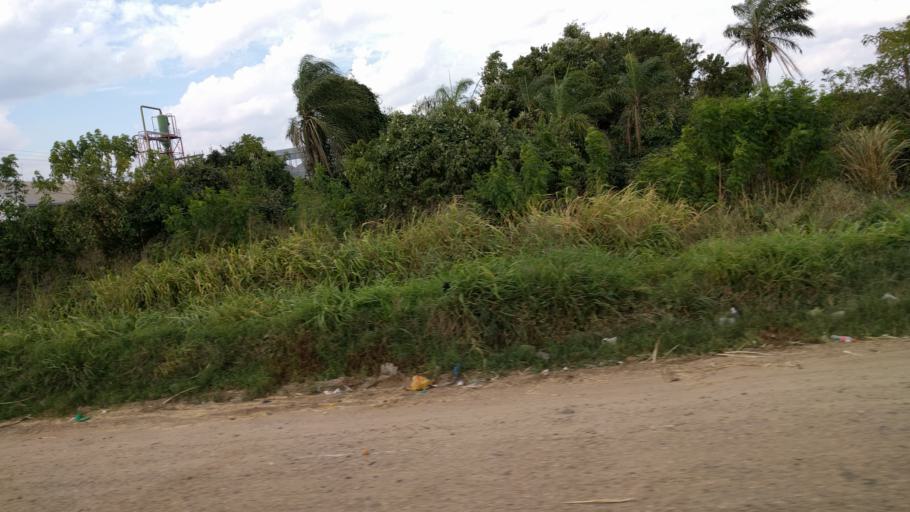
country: BO
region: Santa Cruz
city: Warnes
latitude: -17.5385
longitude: -63.1608
